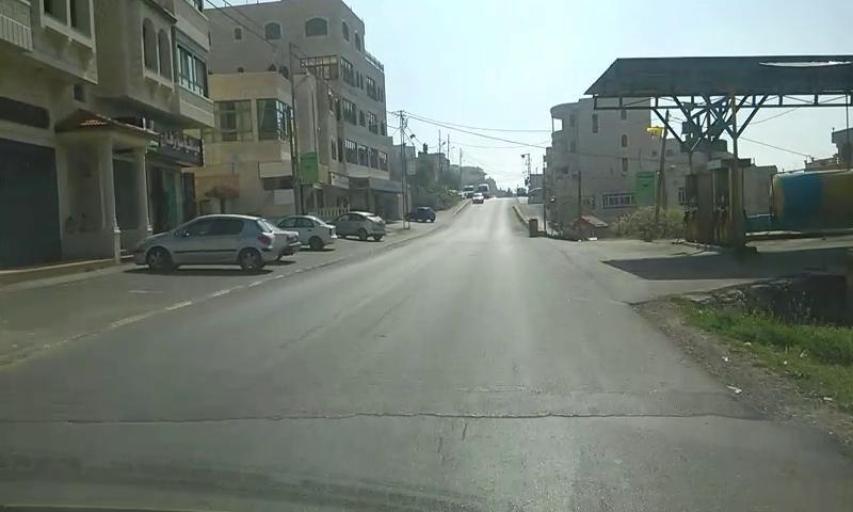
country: PS
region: West Bank
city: Dayr Jarir
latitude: 31.9699
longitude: 35.2880
